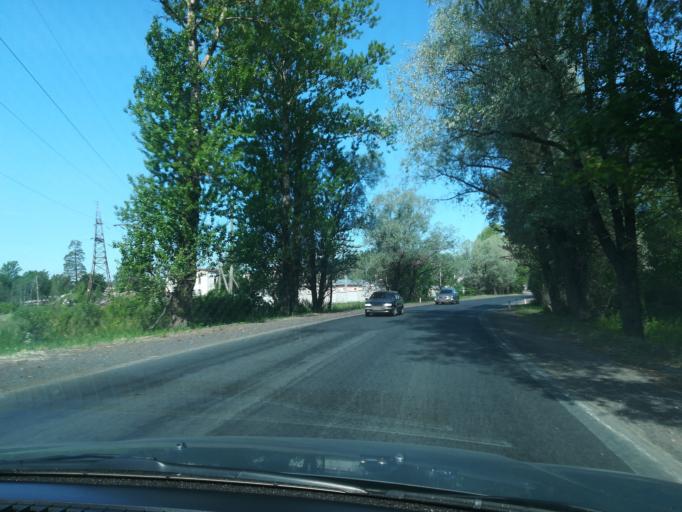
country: RU
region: Leningrad
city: Lesogorskiy
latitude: 61.0781
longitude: 28.9227
